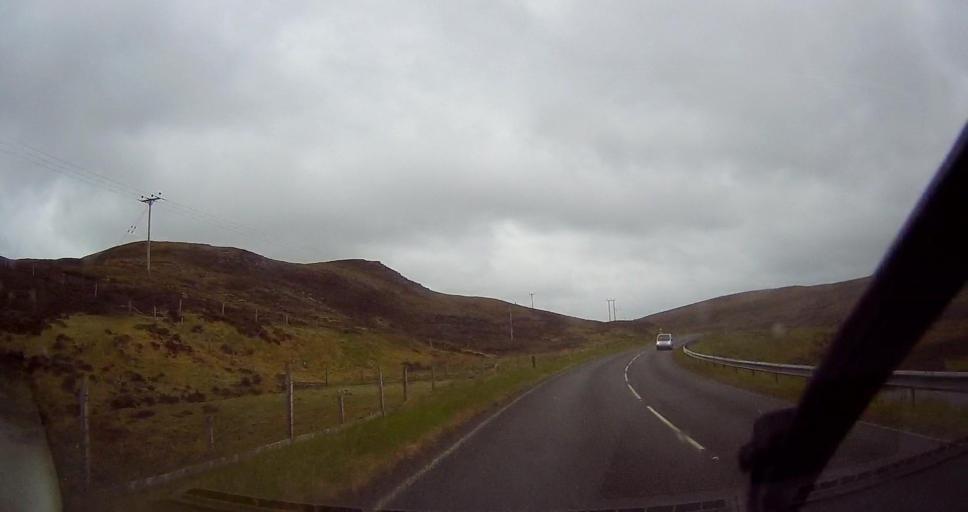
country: GB
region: Scotland
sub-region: Shetland Islands
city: Lerwick
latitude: 60.4426
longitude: -1.3953
